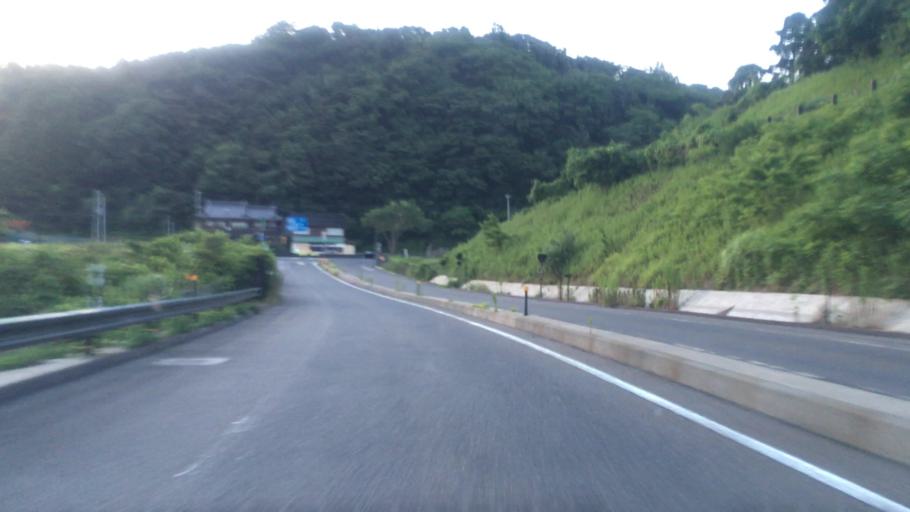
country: JP
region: Tottori
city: Tottori
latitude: 35.6137
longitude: 134.3937
